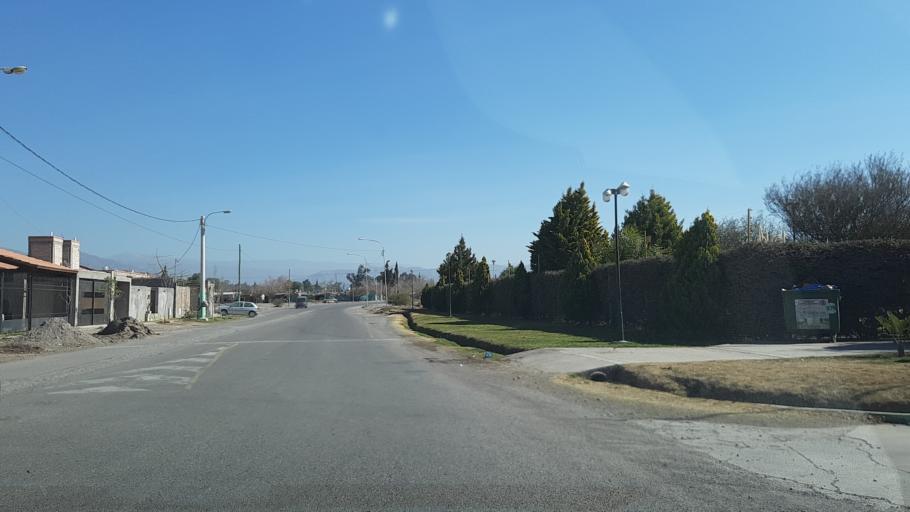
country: AR
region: San Juan
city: San Juan
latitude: -31.5364
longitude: -68.5830
